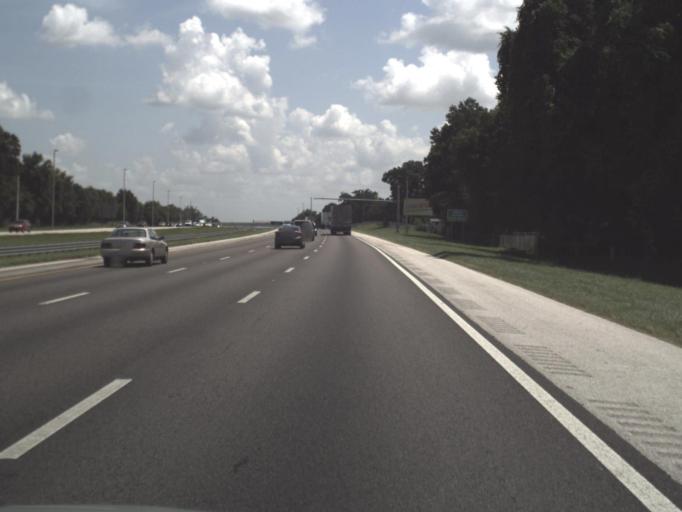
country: US
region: Florida
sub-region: Hillsborough County
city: Seffner
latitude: 28.0094
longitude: -82.2849
